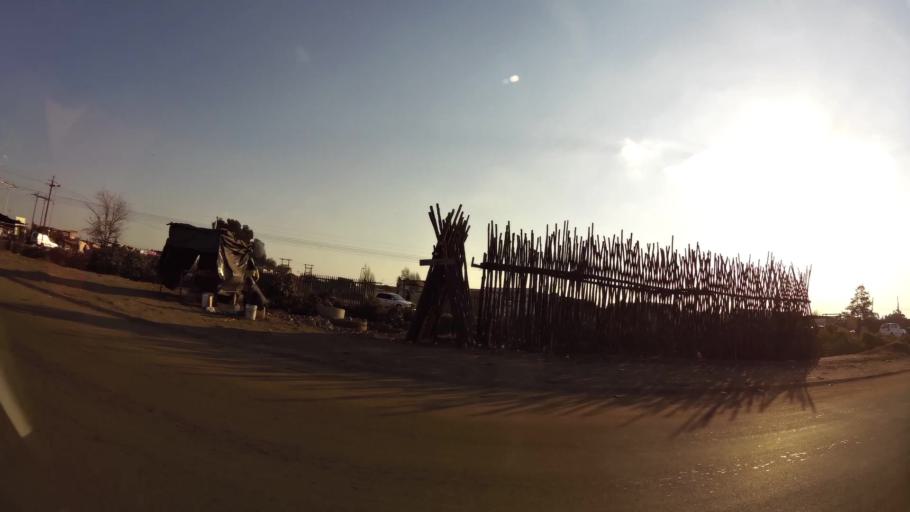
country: ZA
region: Gauteng
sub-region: Ekurhuleni Metropolitan Municipality
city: Tembisa
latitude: -25.9807
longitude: 28.2123
